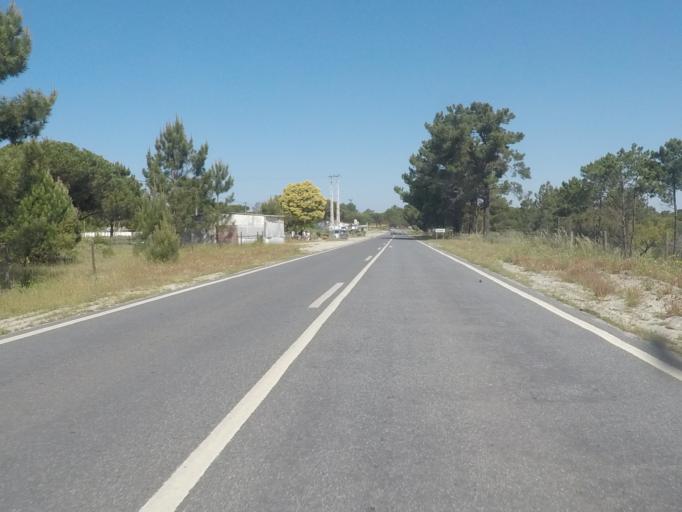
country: PT
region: Setubal
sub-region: Grandola
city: Grandola
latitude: 38.3061
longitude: -8.7387
